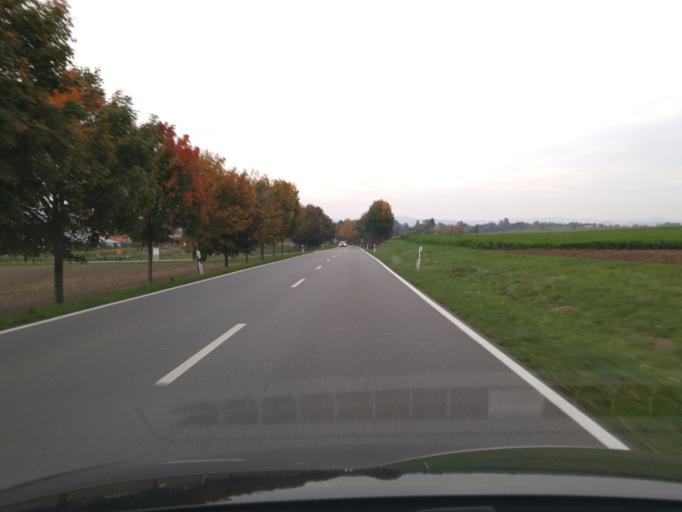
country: DE
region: Baden-Wuerttemberg
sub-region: Regierungsbezirk Stuttgart
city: Bretzfeld
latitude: 49.1757
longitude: 9.4195
